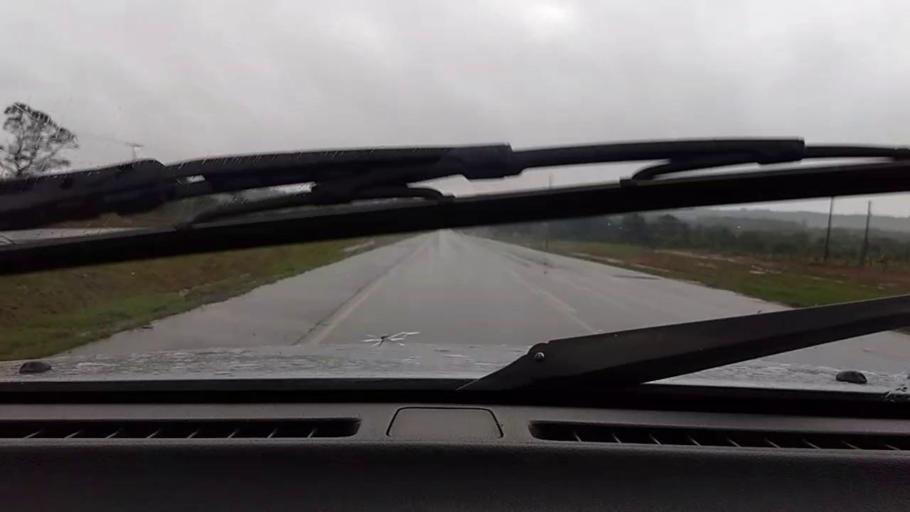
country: PY
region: Caaguazu
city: Repatriacion
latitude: -25.4658
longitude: -55.9508
